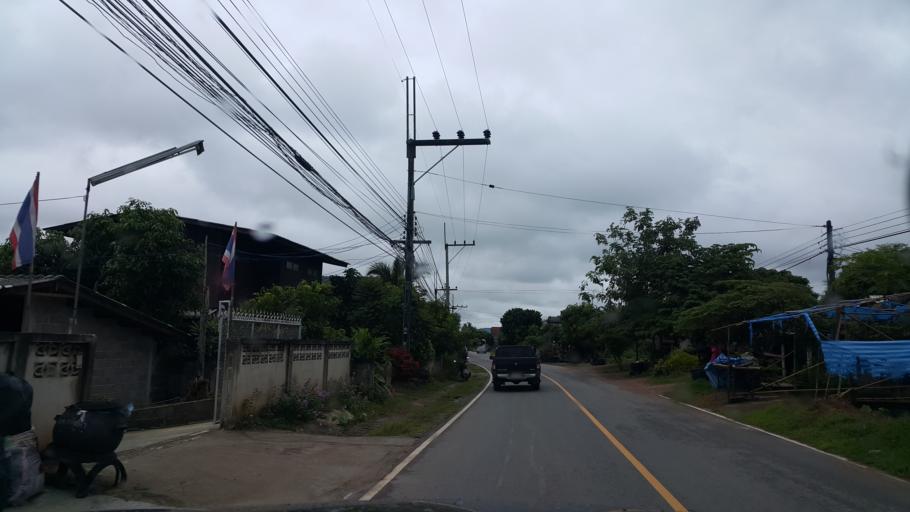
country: TH
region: Phayao
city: Chiang Kham
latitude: 19.5230
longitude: 100.3439
